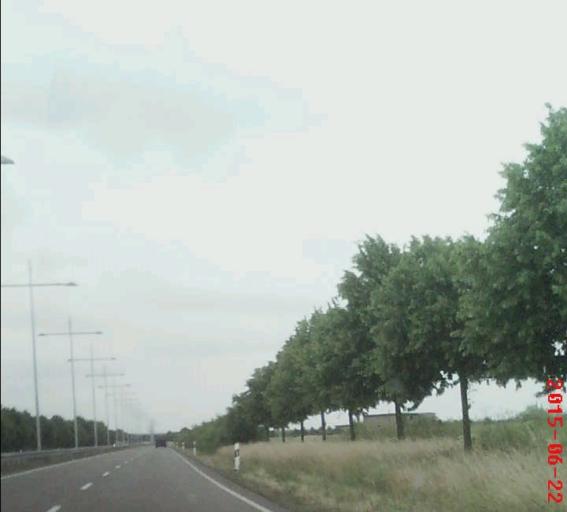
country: DE
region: Saxony
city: Schkeuditz
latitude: 51.4216
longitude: 12.2319
